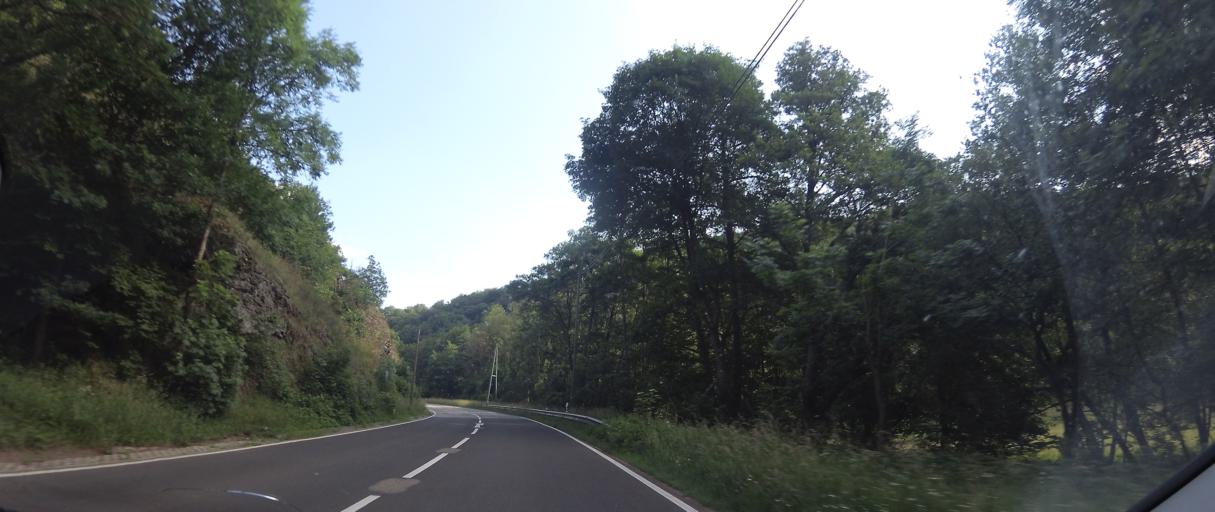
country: DE
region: Rheinland-Pfalz
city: Rathsweiler
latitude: 49.6104
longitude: 7.4601
